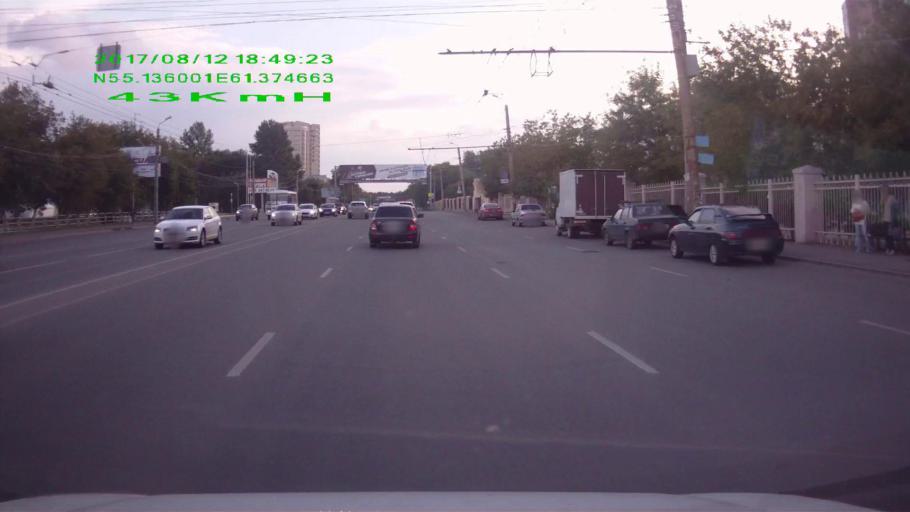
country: RU
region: Chelyabinsk
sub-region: Gorod Chelyabinsk
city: Chelyabinsk
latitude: 55.1329
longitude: 61.3699
